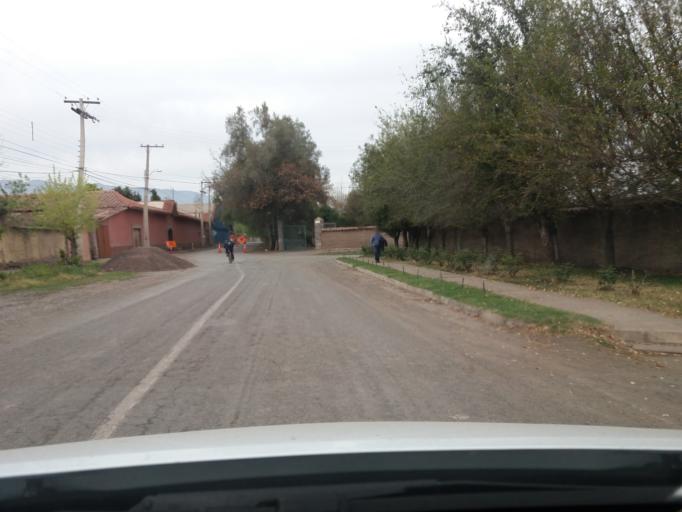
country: CL
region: Valparaiso
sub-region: Provincia de Los Andes
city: Los Andes
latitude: -32.8246
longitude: -70.6475
